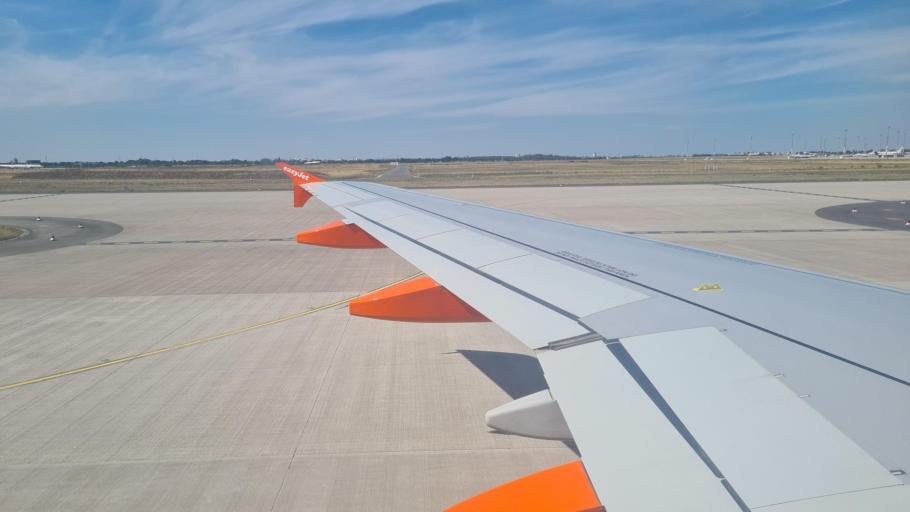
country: DE
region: Brandenburg
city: Schonefeld
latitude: 52.3541
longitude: 13.4950
